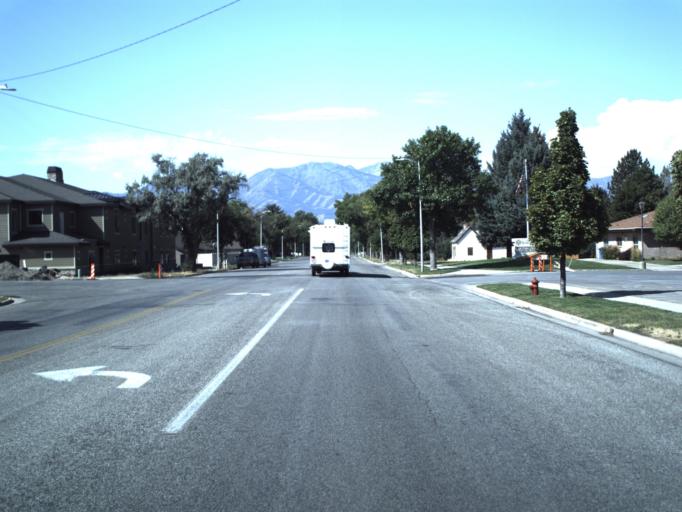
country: US
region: Utah
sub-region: Cache County
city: Hyrum
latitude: 41.6337
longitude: -111.8351
